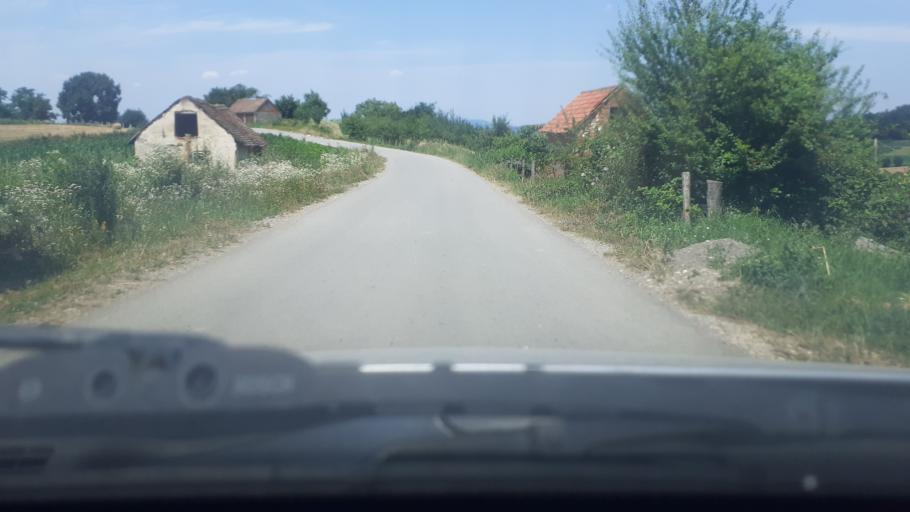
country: RS
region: Central Serbia
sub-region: Kolubarski Okrug
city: Osecina
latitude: 44.3888
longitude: 19.5016
